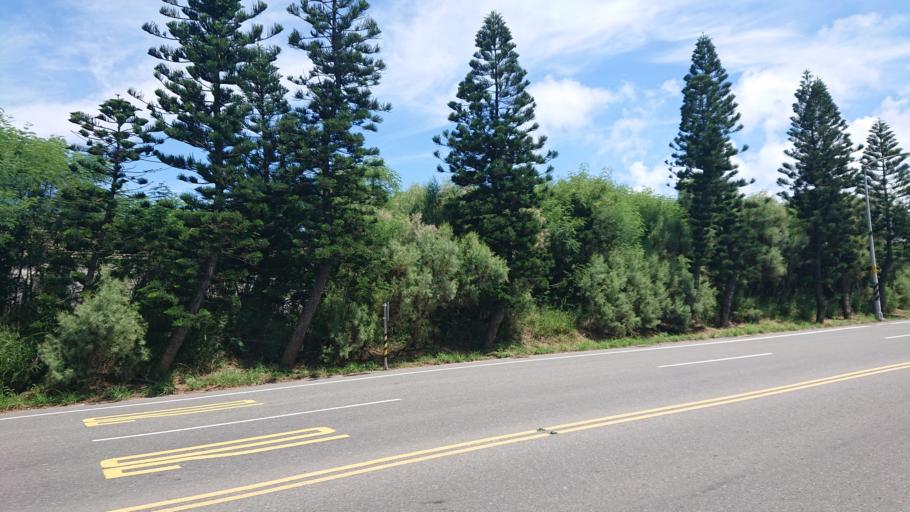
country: TW
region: Taiwan
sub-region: Penghu
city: Ma-kung
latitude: 23.6607
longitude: 119.5576
